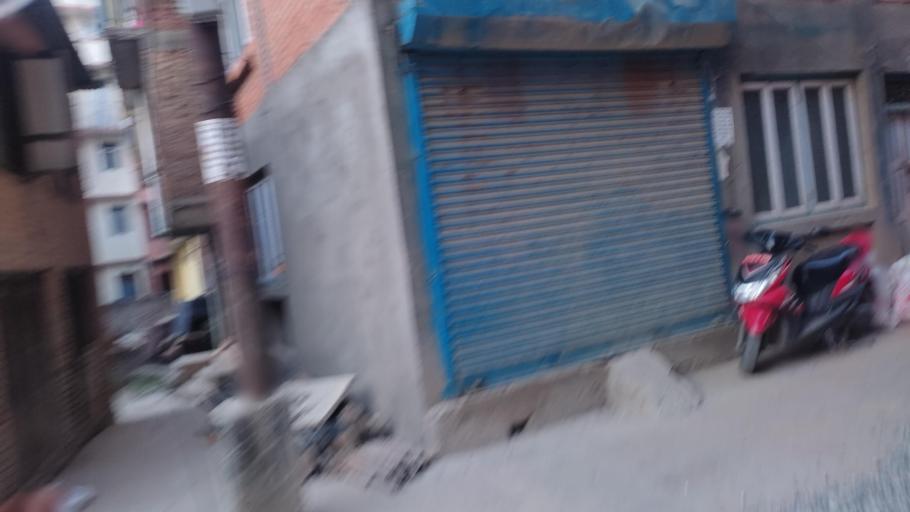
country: NP
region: Central Region
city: Kirtipur
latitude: 27.6706
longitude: 85.2781
